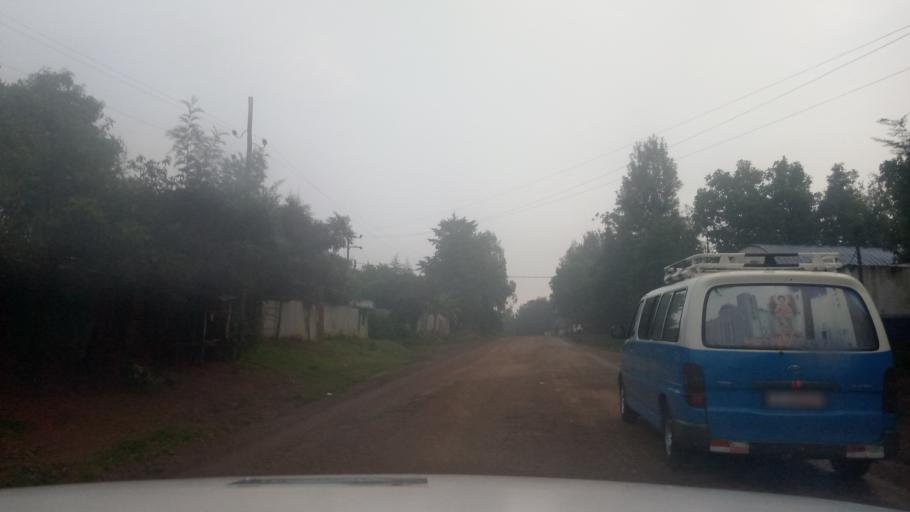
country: ET
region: Oromiya
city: Jima
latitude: 7.6969
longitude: 36.8162
